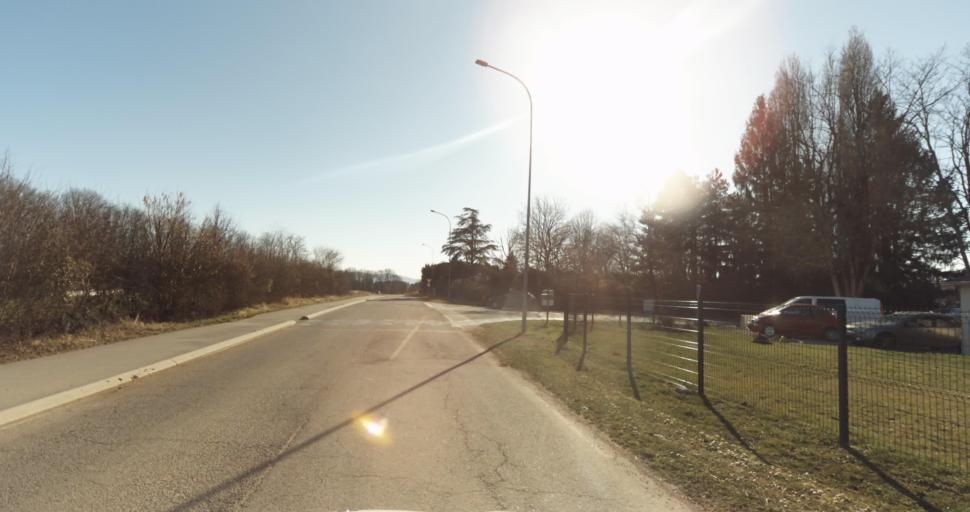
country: FR
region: Franche-Comte
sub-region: Departement du Jura
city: Montmorot
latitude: 46.6867
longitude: 5.5083
